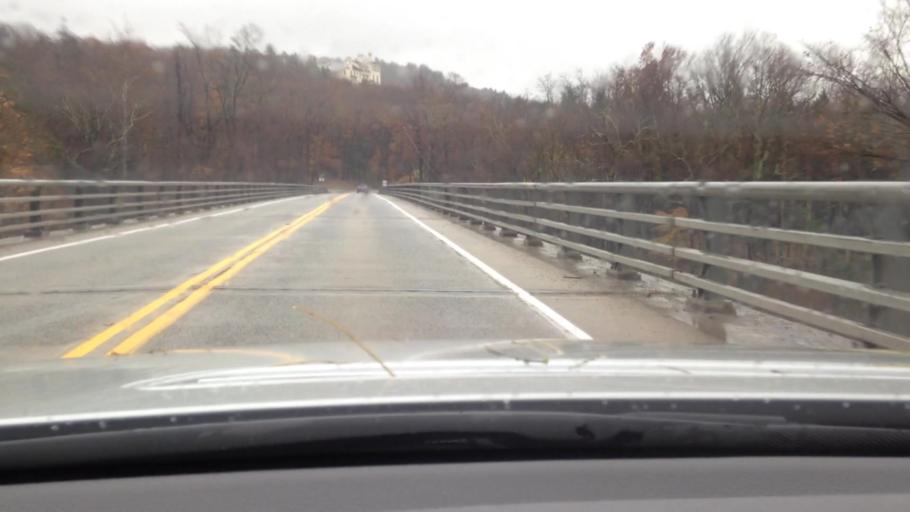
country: US
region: New York
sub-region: Putnam County
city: Cold Spring
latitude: 41.4054
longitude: -73.9318
